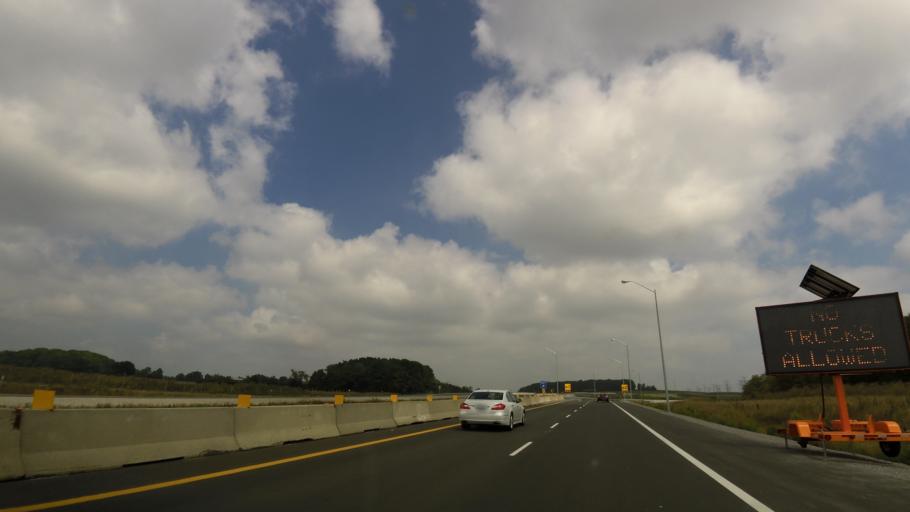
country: CA
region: Ontario
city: Oshawa
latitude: 43.9803
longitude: -78.8765
